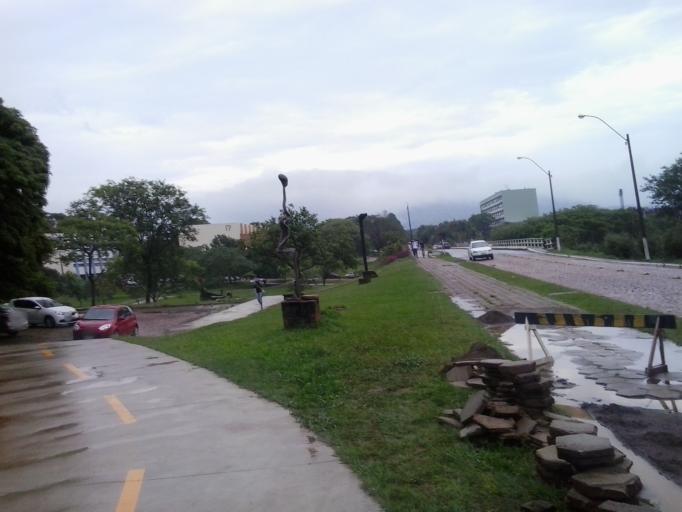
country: BR
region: Rio Grande do Sul
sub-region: Santa Maria
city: Santa Maria
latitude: -29.7181
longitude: -53.7154
